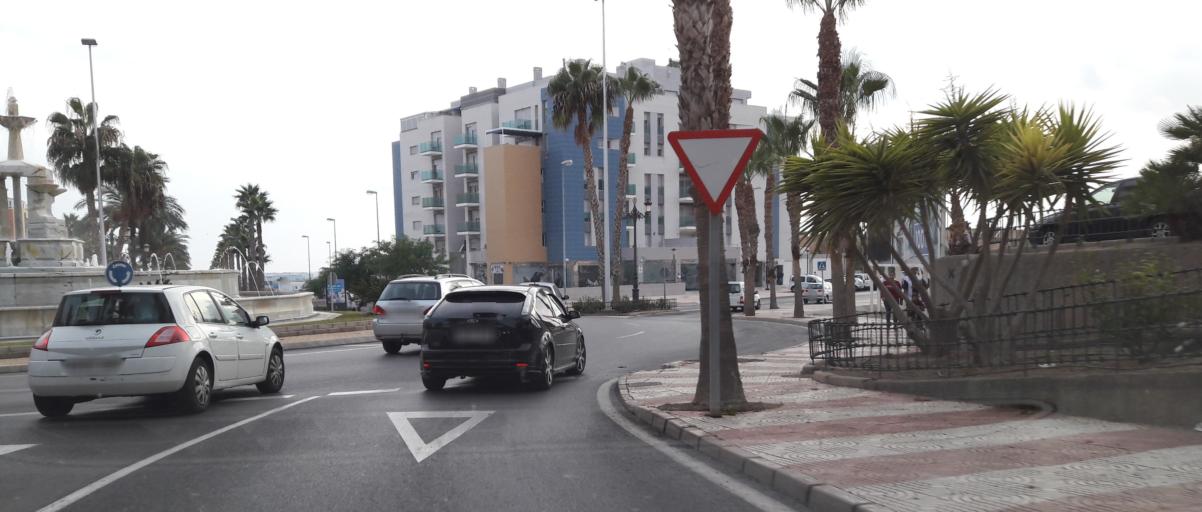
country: ES
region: Andalusia
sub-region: Provincia de Almeria
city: Aguadulce
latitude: 36.8037
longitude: -2.5998
